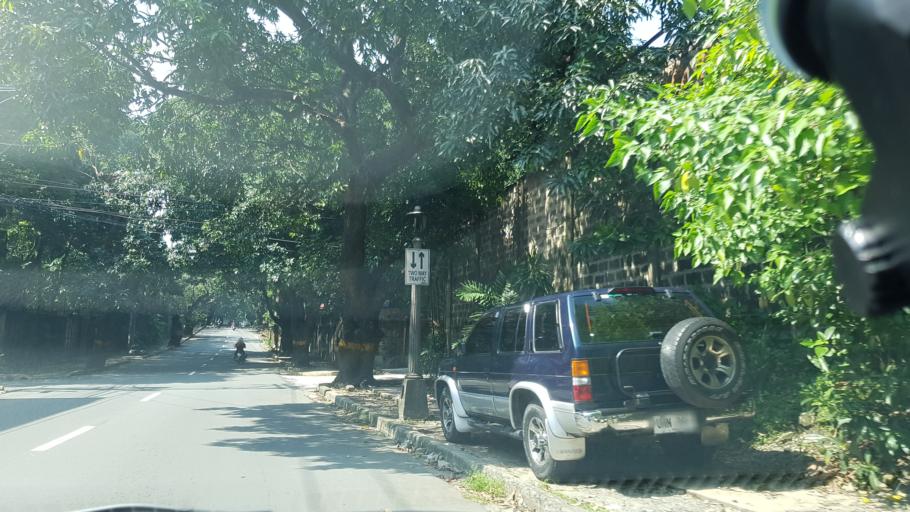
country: PH
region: Metro Manila
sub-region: San Juan
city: San Juan
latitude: 14.6168
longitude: 121.0300
